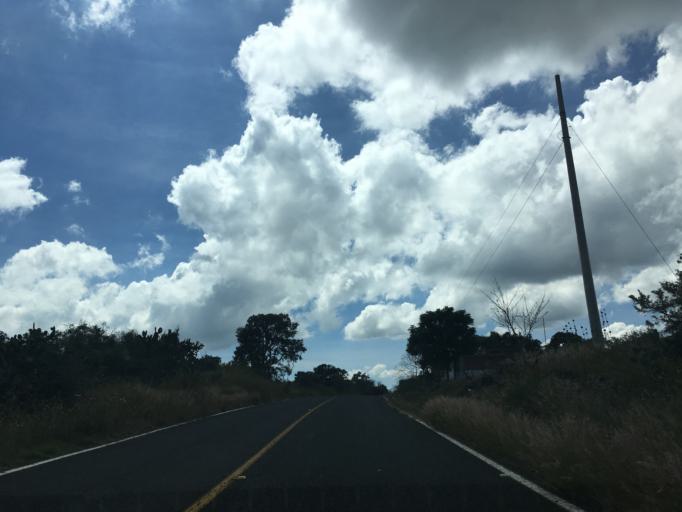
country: MX
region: Michoacan
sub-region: Morelia
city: Cuto de la Esperanza
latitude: 19.7640
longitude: -101.3718
